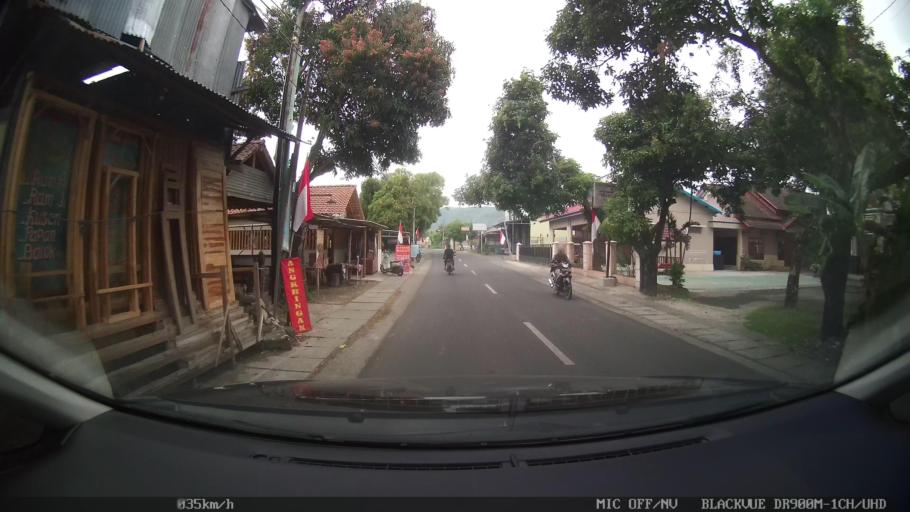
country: ID
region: Daerah Istimewa Yogyakarta
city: Sewon
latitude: -7.8793
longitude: 110.4162
